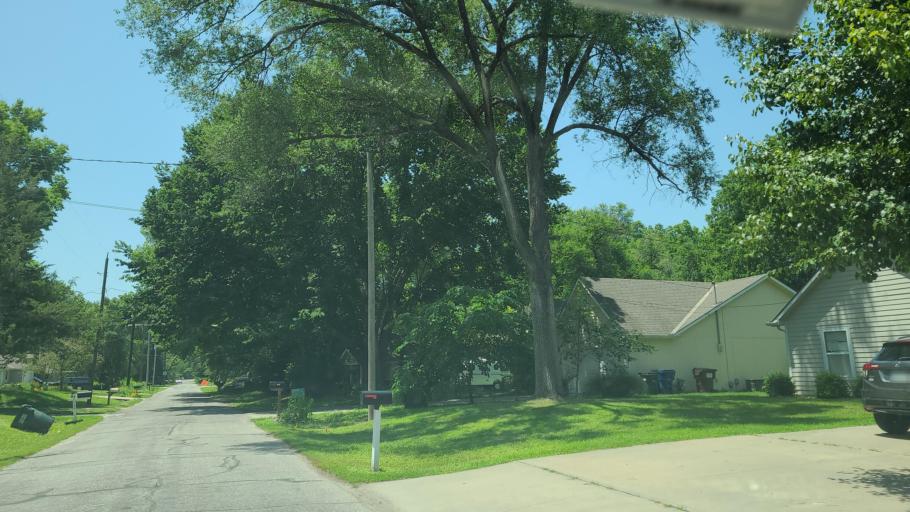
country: US
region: Kansas
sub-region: Douglas County
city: Lawrence
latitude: 38.9751
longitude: -95.2226
